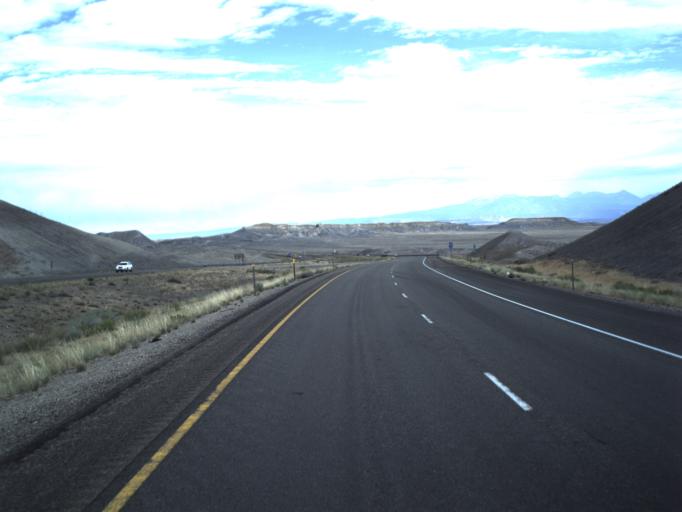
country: US
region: Utah
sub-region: Grand County
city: Moab
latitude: 38.9602
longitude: -109.7136
